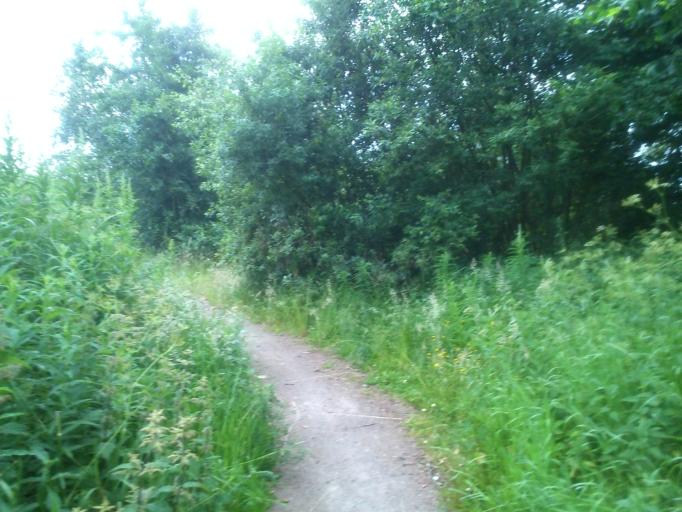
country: DK
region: Central Jutland
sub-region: Ringkobing-Skjern Kommune
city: Tarm
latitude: 55.9026
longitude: 8.5260
